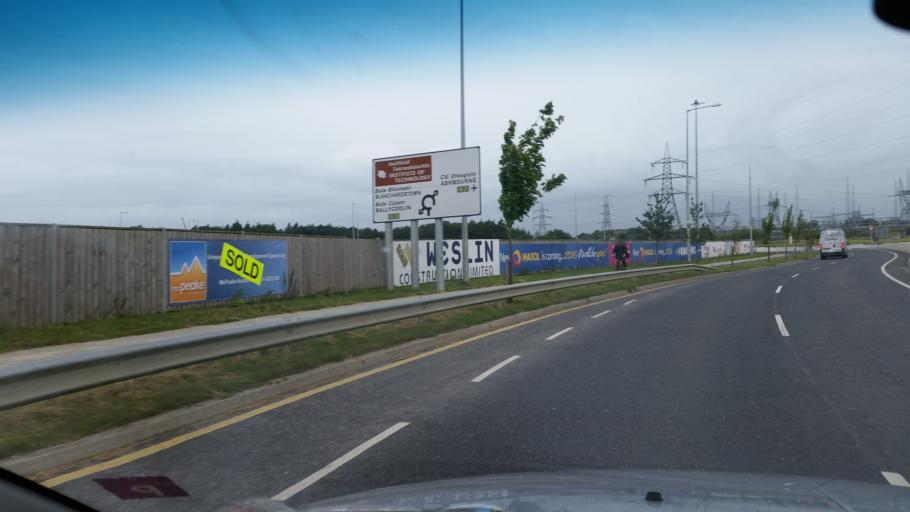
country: IE
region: Leinster
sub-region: Fingal County
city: Blanchardstown
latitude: 53.4156
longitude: -6.3601
